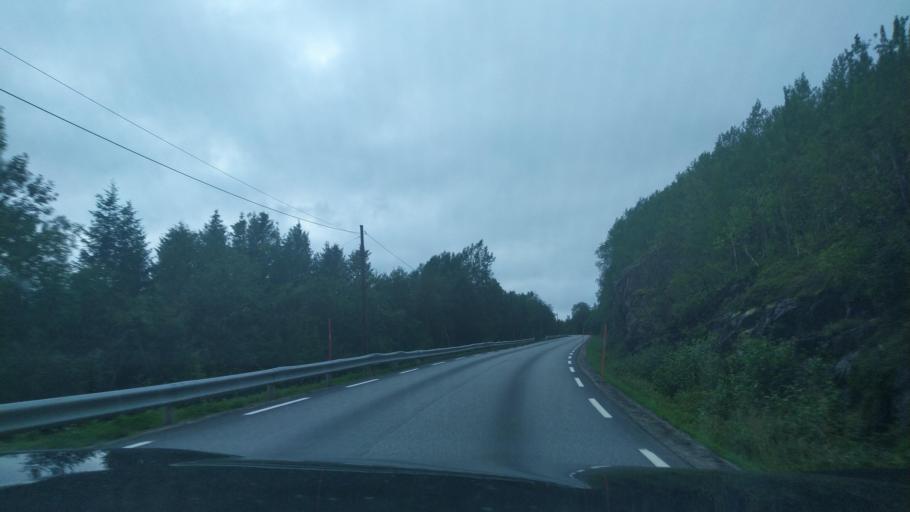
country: NO
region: Troms
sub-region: Lavangen
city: Tennevoll
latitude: 68.7253
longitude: 17.8334
